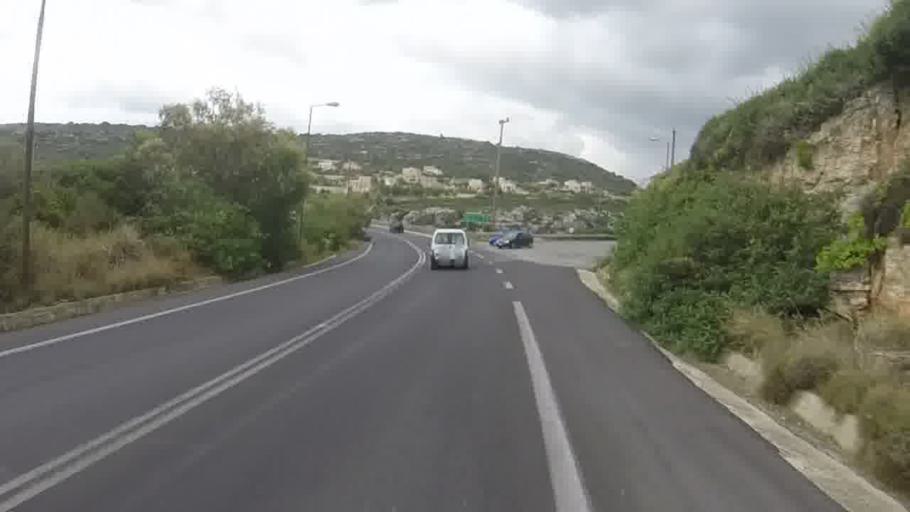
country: GR
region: Crete
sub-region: Nomos Rethymnis
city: Atsipopoulon
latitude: 35.3599
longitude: 24.4059
